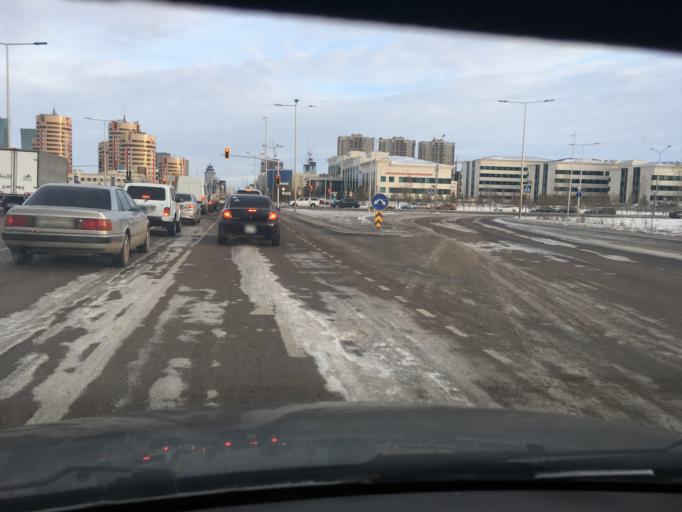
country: KZ
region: Astana Qalasy
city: Astana
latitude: 51.1271
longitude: 71.4031
